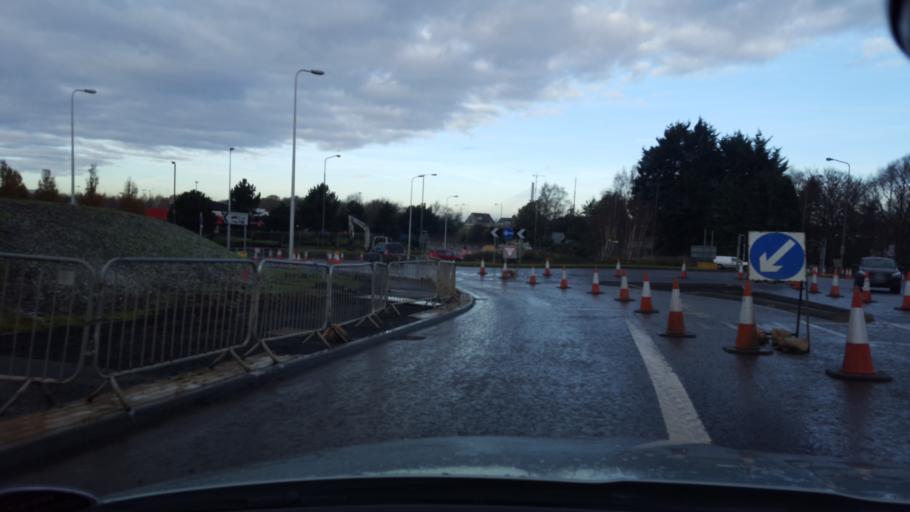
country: GB
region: Scotland
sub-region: Edinburgh
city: Queensferry
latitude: 55.9828
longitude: -3.3965
